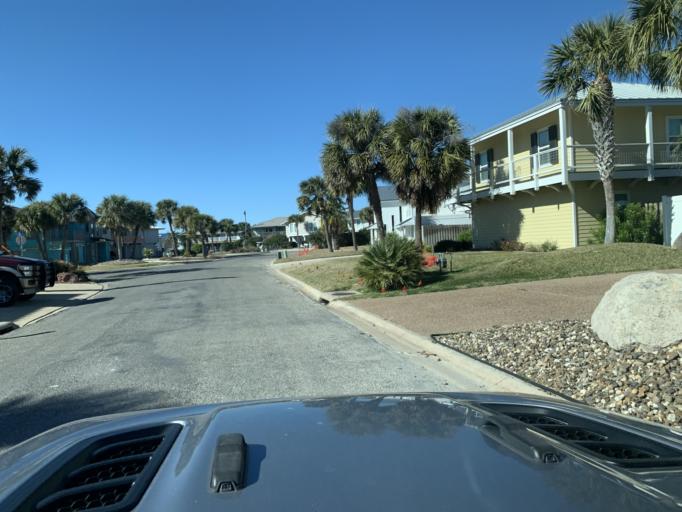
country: US
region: Texas
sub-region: Aransas County
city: Rockport
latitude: 28.0331
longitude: -97.0268
